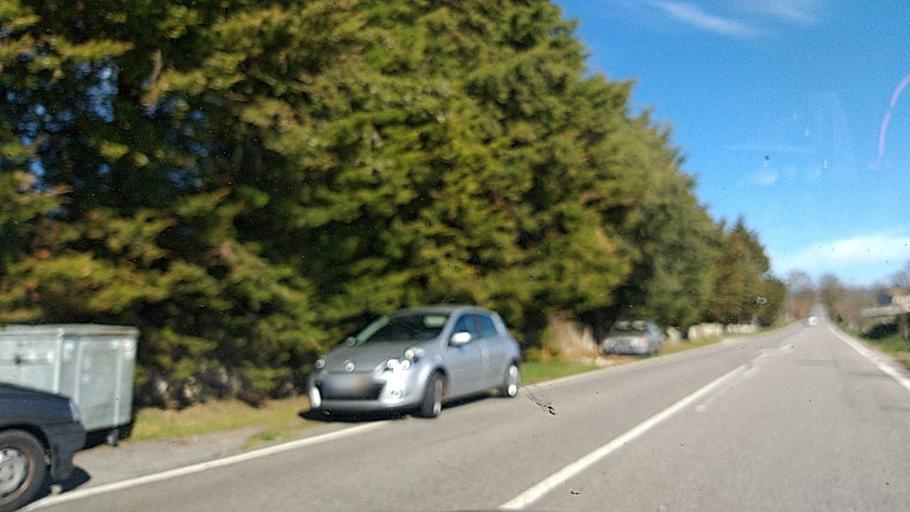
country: PT
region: Guarda
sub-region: Guarda
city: Sequeira
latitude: 40.6007
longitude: -7.1043
